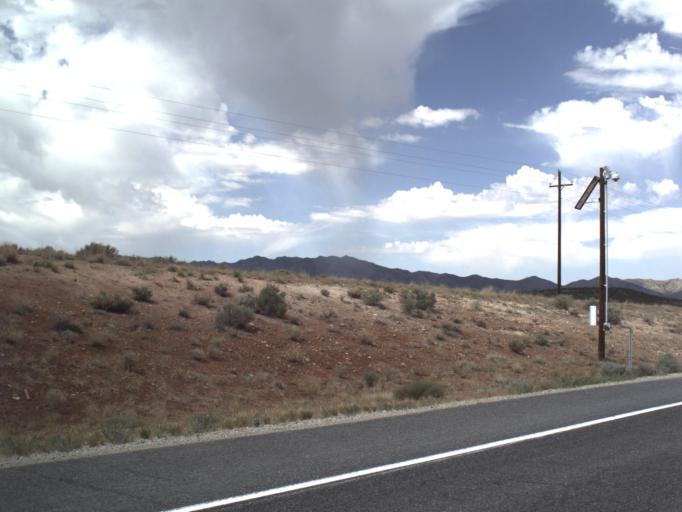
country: US
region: Utah
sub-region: Utah County
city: Eagle Mountain
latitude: 40.0720
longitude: -112.3693
